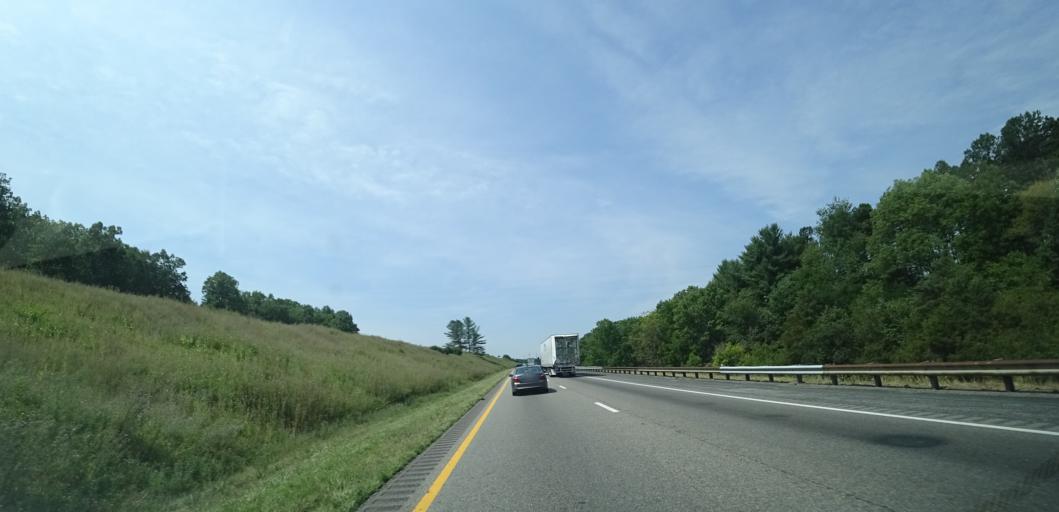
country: US
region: Virginia
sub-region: City of Staunton
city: Staunton
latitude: 38.1371
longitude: -79.0252
